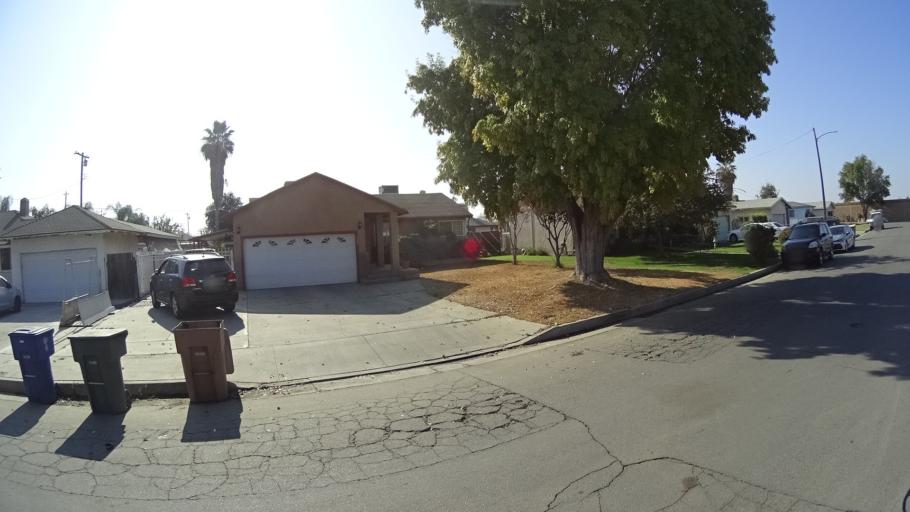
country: US
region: California
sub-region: Kern County
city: Bakersfield
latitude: 35.3504
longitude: -119.0371
